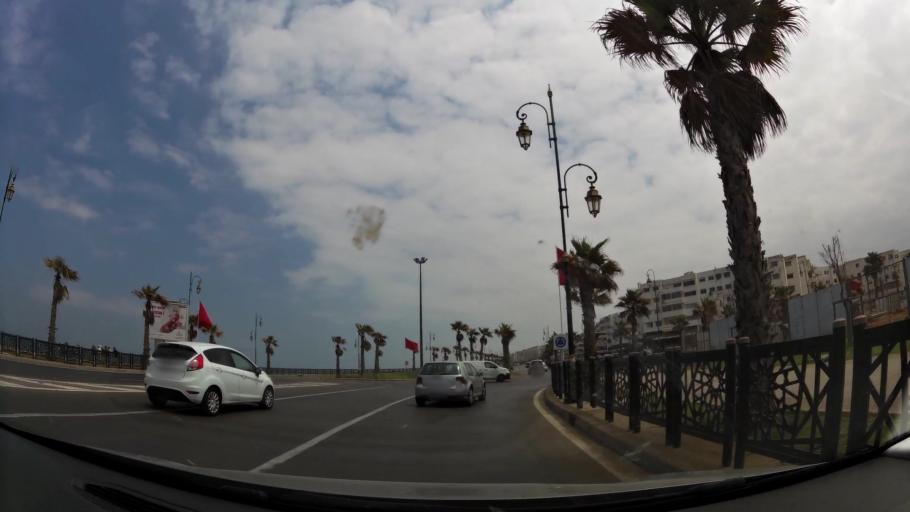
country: MA
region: Rabat-Sale-Zemmour-Zaer
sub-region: Rabat
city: Rabat
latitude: 33.9912
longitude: -6.8850
